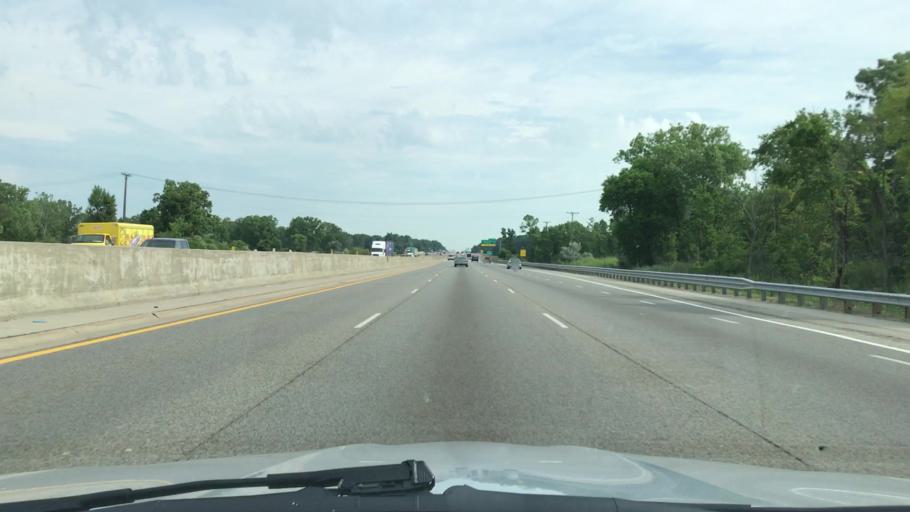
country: US
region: Michigan
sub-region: Macomb County
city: Mount Clemens
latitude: 42.5657
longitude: -82.8588
